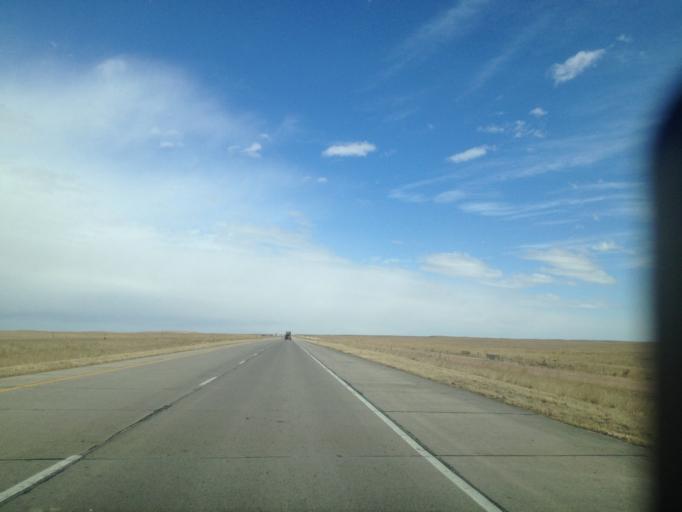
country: US
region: Colorado
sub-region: Weld County
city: Keenesburg
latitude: 40.1748
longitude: -104.3321
